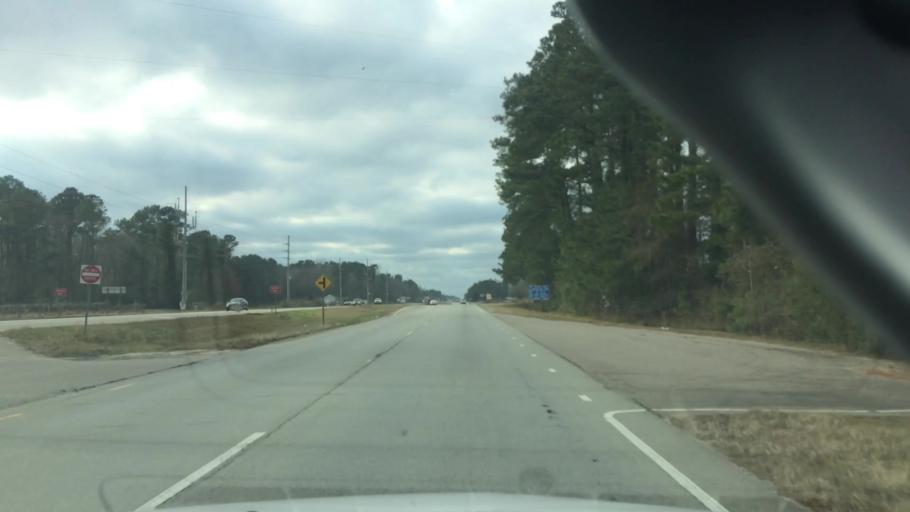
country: US
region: North Carolina
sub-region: Brunswick County
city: Shallotte
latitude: 33.9553
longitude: -78.4452
